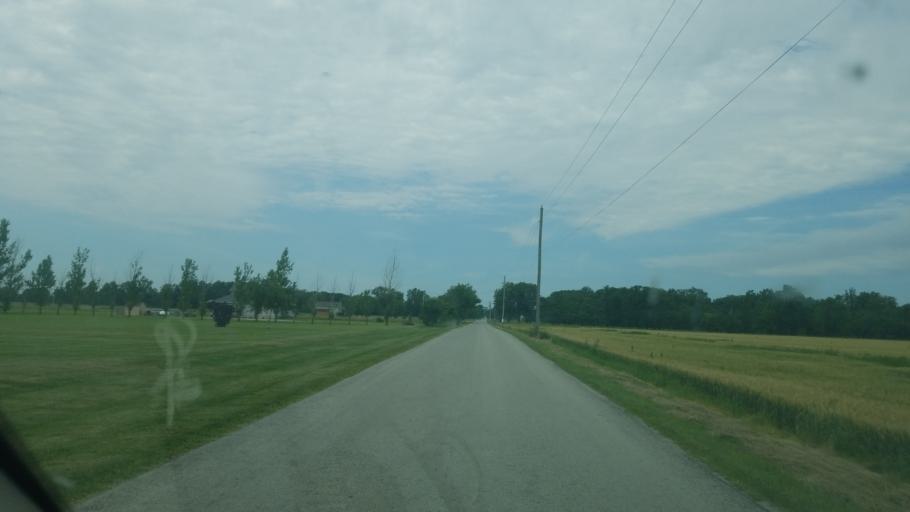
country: US
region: Ohio
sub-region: Wood County
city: North Baltimore
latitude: 41.2220
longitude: -83.6269
